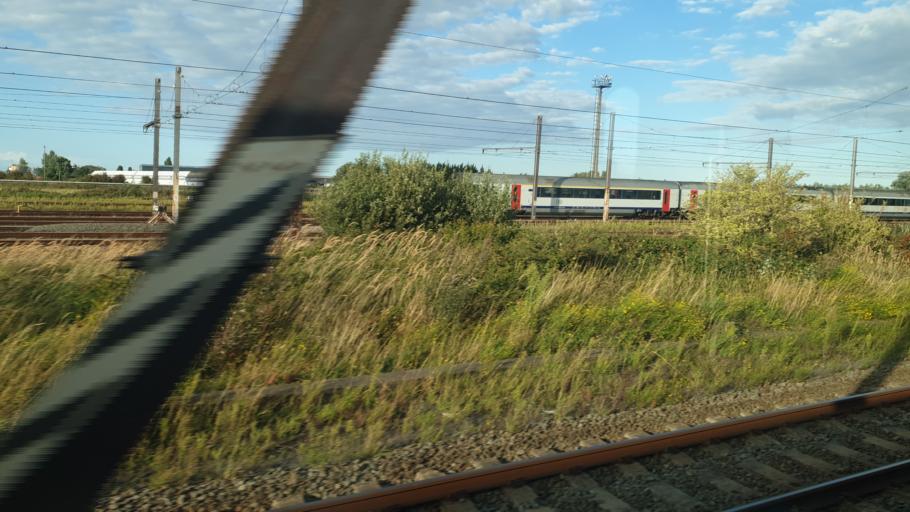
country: BE
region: Flanders
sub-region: Provincie West-Vlaanderen
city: Bredene
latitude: 51.2134
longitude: 2.9621
